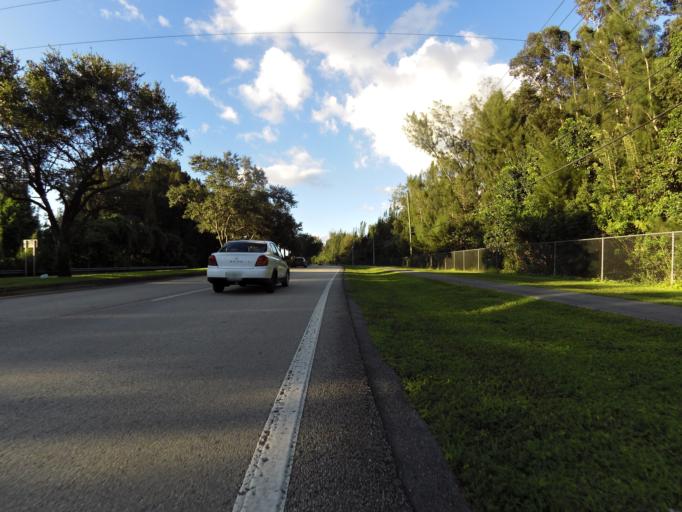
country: US
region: Florida
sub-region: Broward County
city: Cooper City
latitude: 26.0671
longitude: -80.2803
